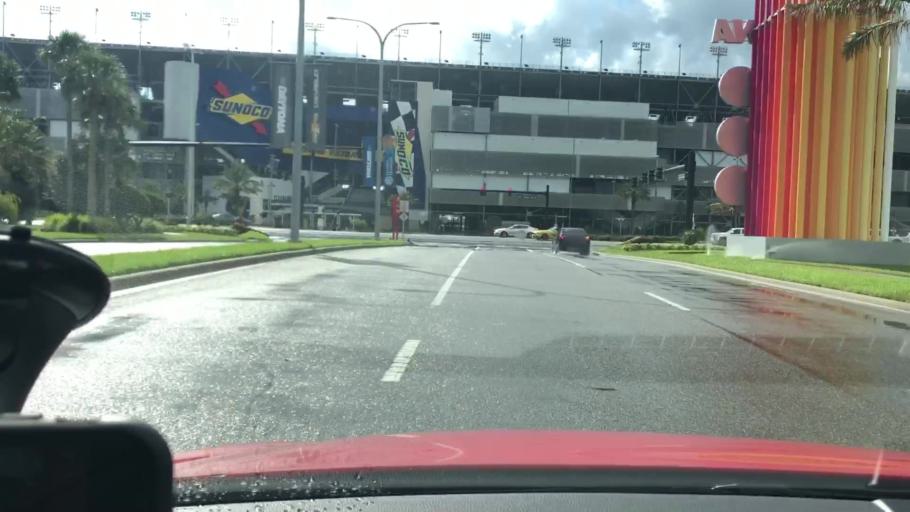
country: US
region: Florida
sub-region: Volusia County
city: Daytona Beach
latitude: 29.1924
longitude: -81.0710
